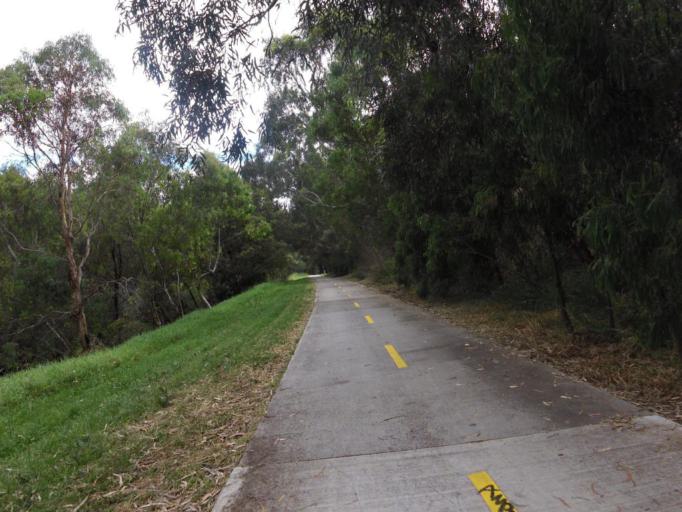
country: AU
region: Victoria
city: Heidelberg West
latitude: -37.7502
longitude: 145.0321
